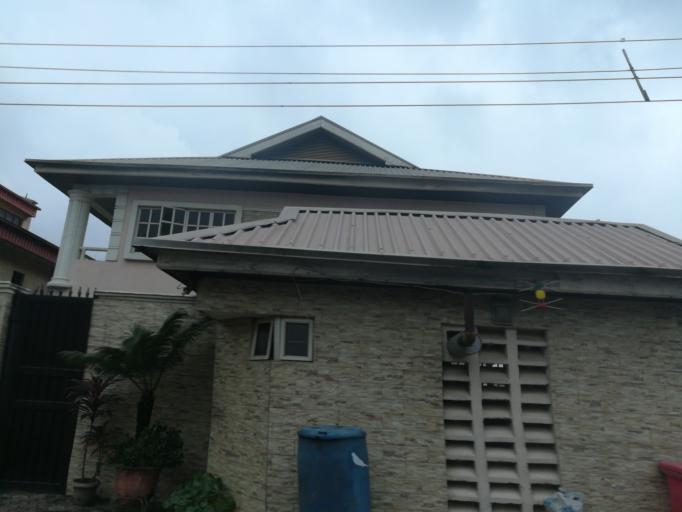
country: NG
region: Lagos
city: Ojota
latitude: 6.5684
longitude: 3.3739
